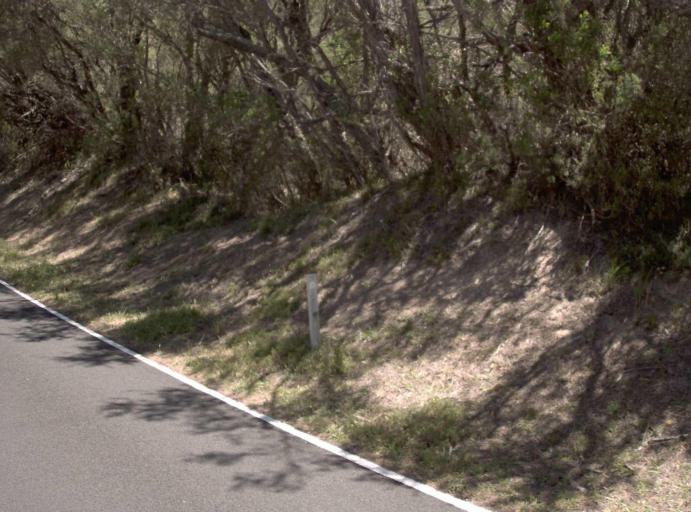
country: AU
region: Victoria
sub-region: Latrobe
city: Morwell
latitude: -38.8815
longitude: 146.2640
